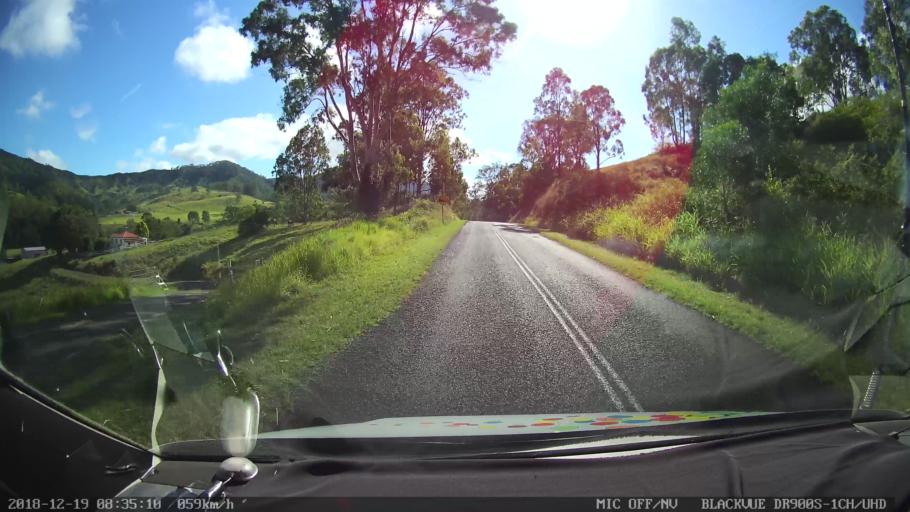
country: AU
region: New South Wales
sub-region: Kyogle
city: Kyogle
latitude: -28.3218
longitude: 152.9670
